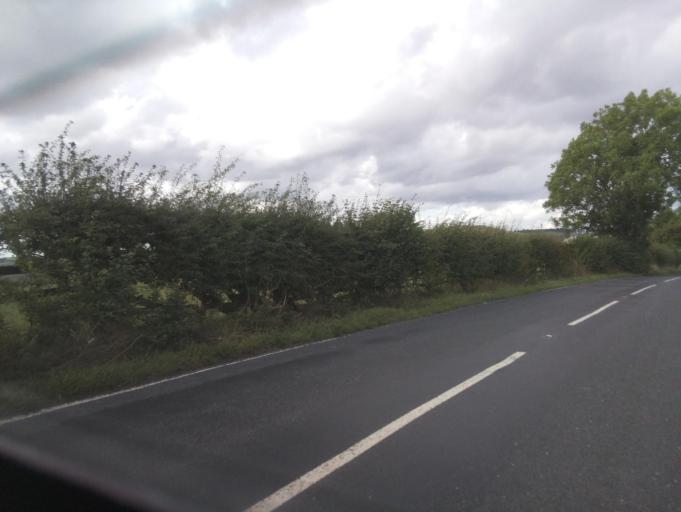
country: GB
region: England
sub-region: North Yorkshire
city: Leyburn
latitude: 54.3737
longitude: -1.8295
